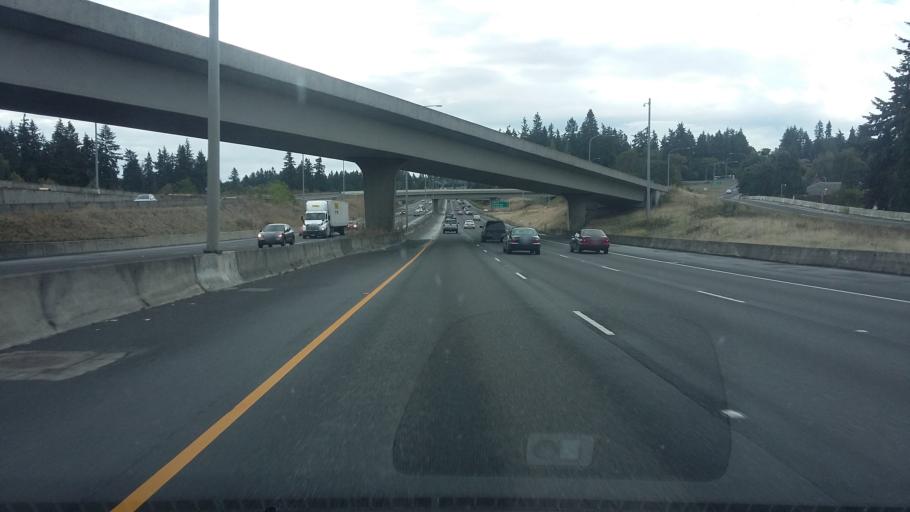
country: US
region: Washington
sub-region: Clark County
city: Hazel Dell
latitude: 45.6605
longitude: -122.6660
